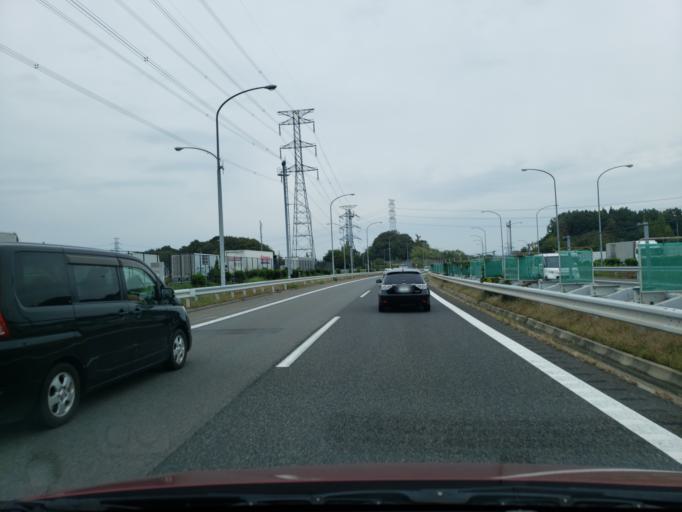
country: JP
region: Hyogo
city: Sandacho
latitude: 34.8307
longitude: 135.1542
